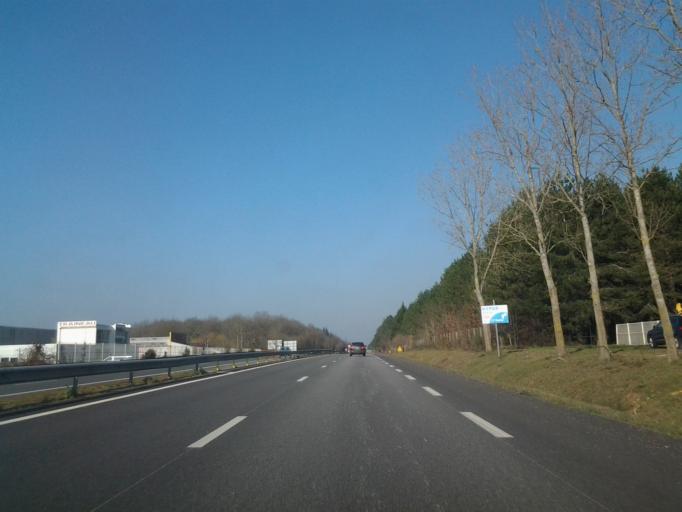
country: FR
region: Pays de la Loire
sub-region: Departement de la Vendee
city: Aizenay
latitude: 46.7254
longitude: -1.5667
